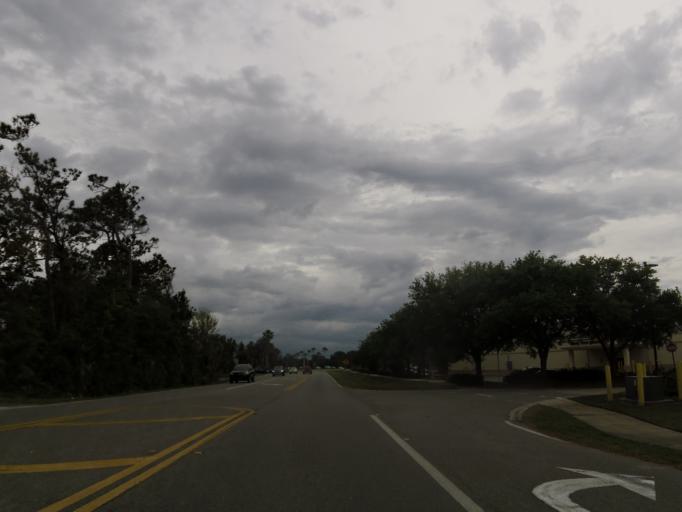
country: US
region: Florida
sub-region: Saint Johns County
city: Sawgrass
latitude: 30.1926
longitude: -81.3818
